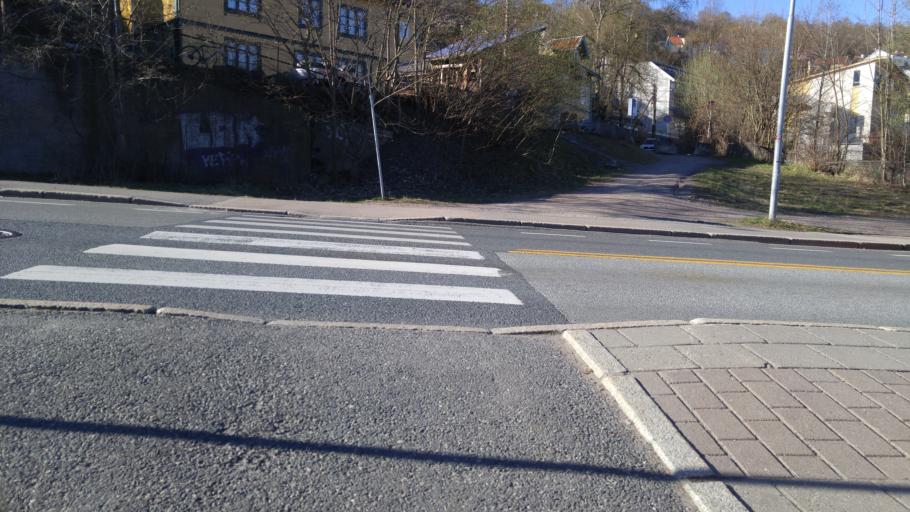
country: NO
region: Oslo
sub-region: Oslo
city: Oslo
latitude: 59.9034
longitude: 10.7781
